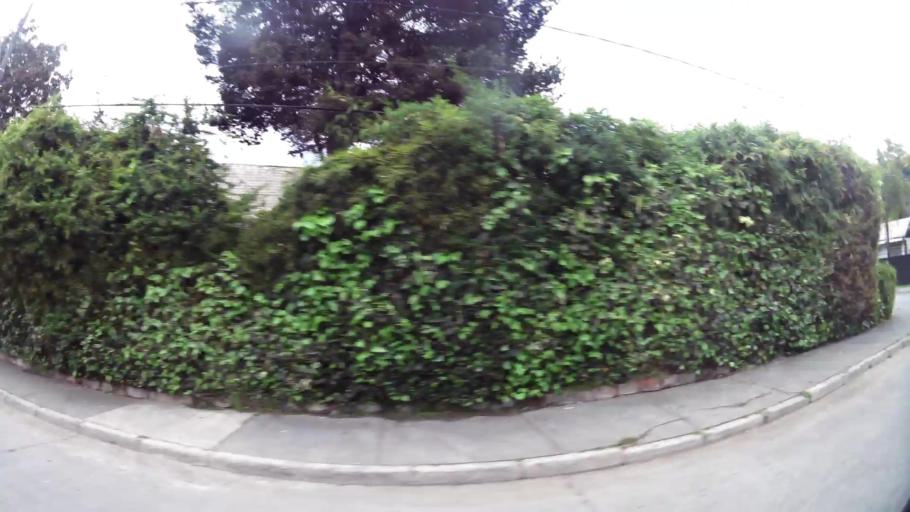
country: CL
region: Santiago Metropolitan
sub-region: Provincia de Santiago
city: Villa Presidente Frei, Nunoa, Santiago, Chile
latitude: -33.4129
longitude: -70.6104
